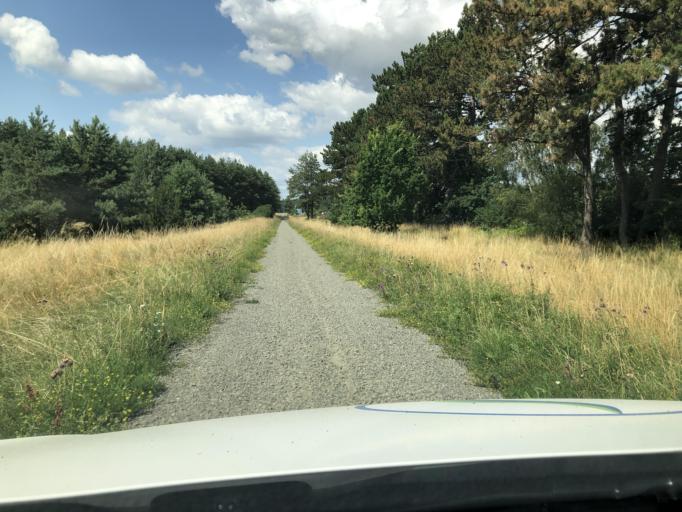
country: SE
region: Skane
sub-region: Kristianstads Kommun
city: Degeberga
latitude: 55.8502
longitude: 14.0929
